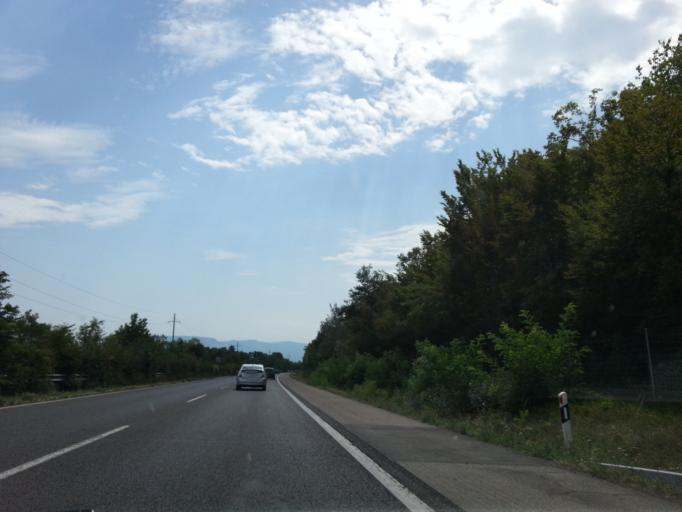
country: CH
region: Geneva
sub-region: Geneva
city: Versoix
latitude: 46.2934
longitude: 6.1461
